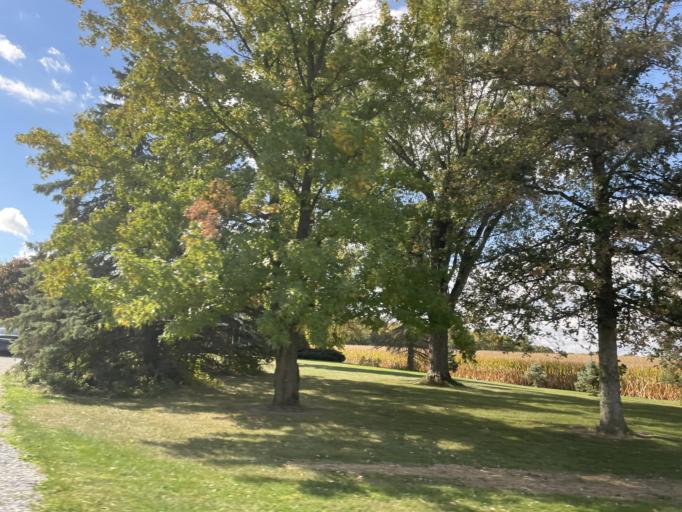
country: US
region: Indiana
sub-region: Allen County
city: Fort Wayne
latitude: 41.1161
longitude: -85.2322
